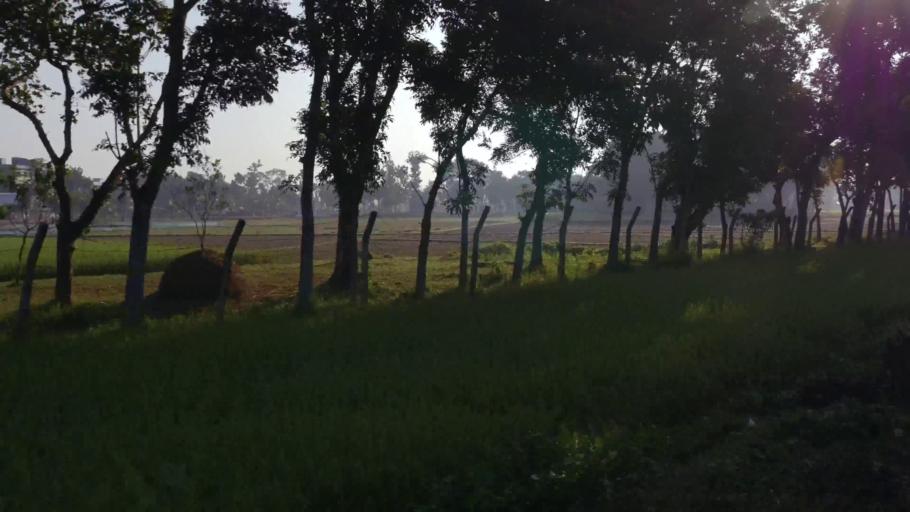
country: BD
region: Dhaka
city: Jamalpur
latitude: 24.9124
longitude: 89.9595
